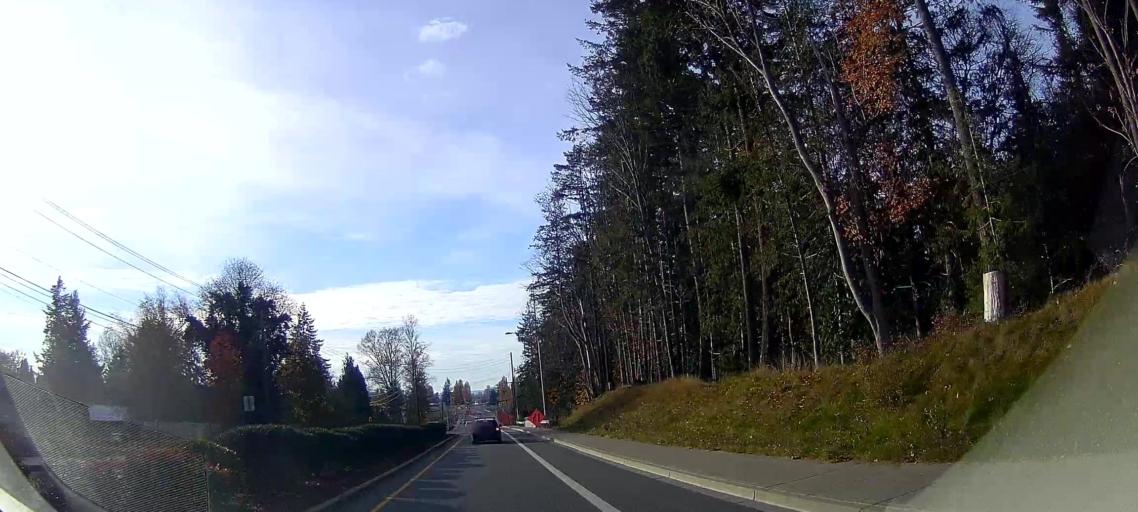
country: US
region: Washington
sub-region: Skagit County
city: Mount Vernon
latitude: 48.3995
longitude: -122.3218
